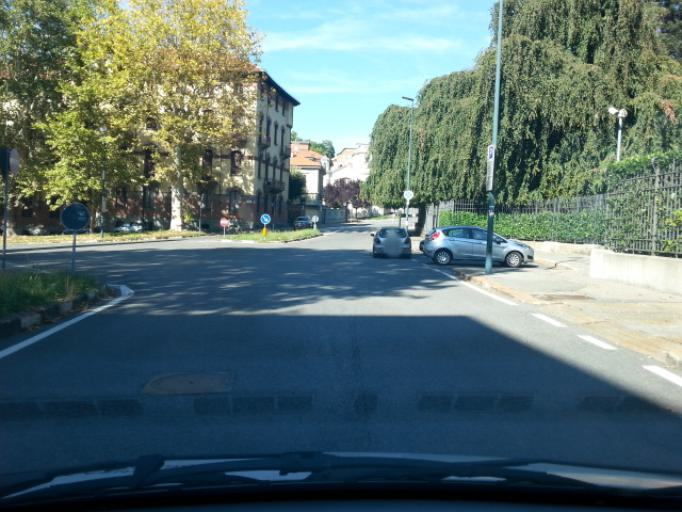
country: IT
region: Piedmont
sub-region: Provincia di Torino
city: Turin
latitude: 45.0560
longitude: 7.6963
